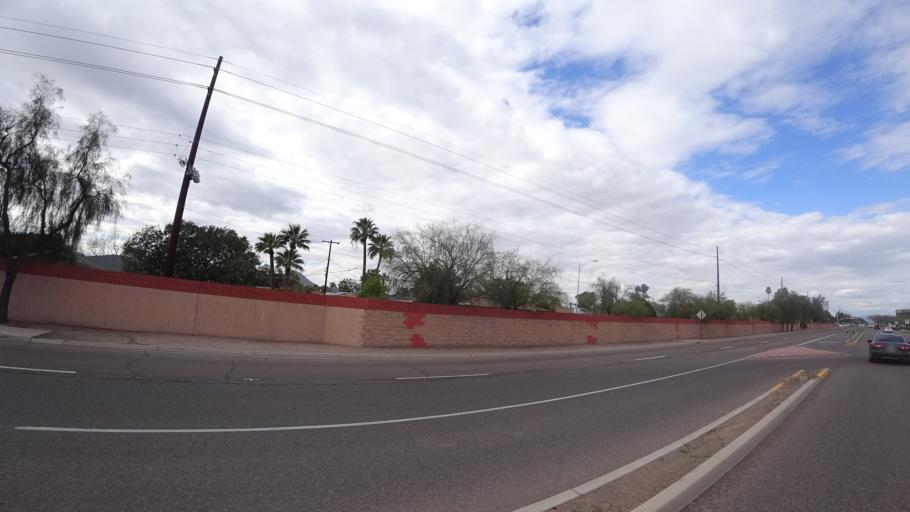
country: US
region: Arizona
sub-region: Maricopa County
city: Scottsdale
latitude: 33.5059
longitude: -111.8916
